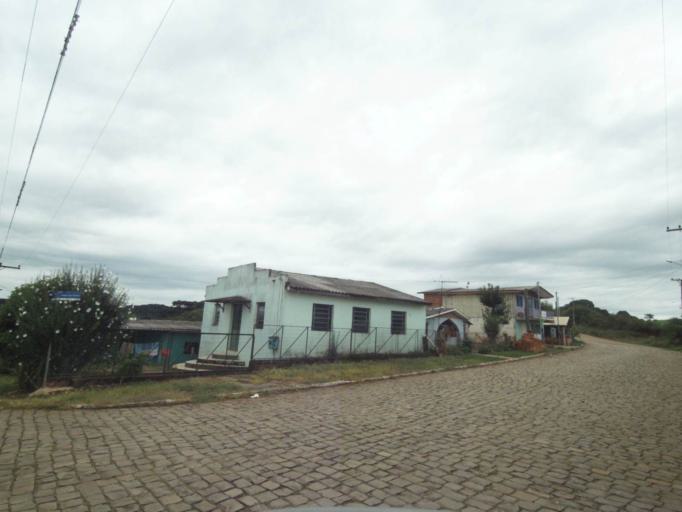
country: BR
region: Rio Grande do Sul
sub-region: Lagoa Vermelha
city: Lagoa Vermelha
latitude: -28.2238
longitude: -51.5390
